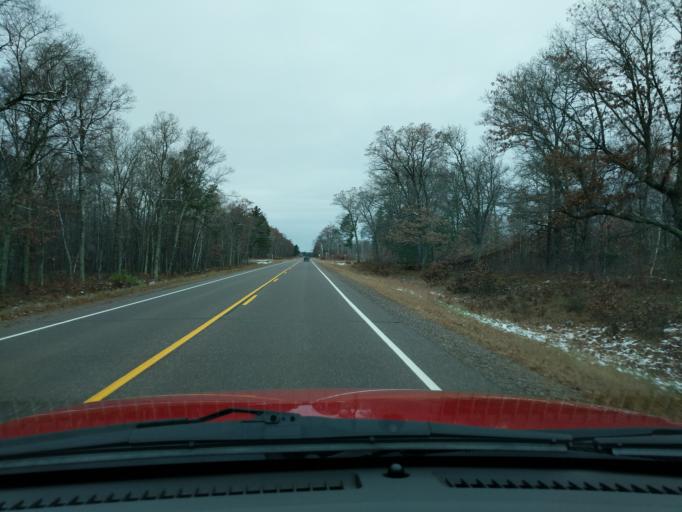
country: US
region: Wisconsin
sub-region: Washburn County
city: Shell Lake
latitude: 45.8149
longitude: -92.1318
